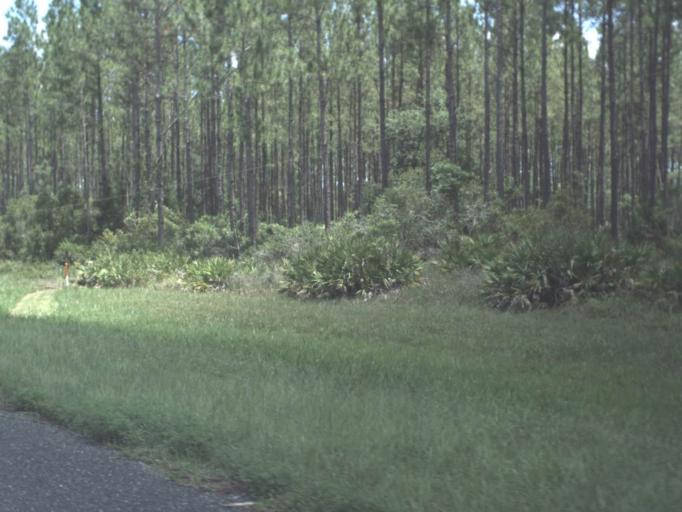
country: US
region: Florida
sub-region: Taylor County
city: Steinhatchee
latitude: 29.7423
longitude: -83.3188
